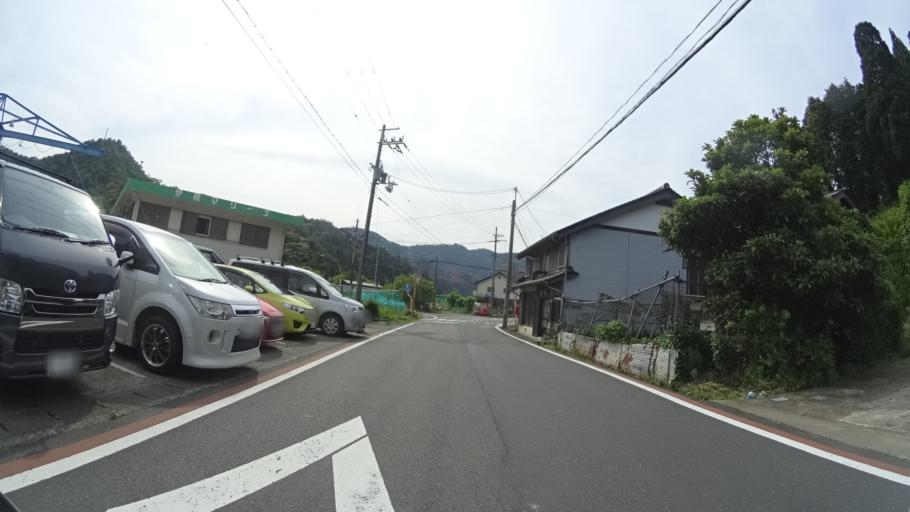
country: JP
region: Kyoto
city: Miyazu
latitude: 35.6720
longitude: 135.2754
